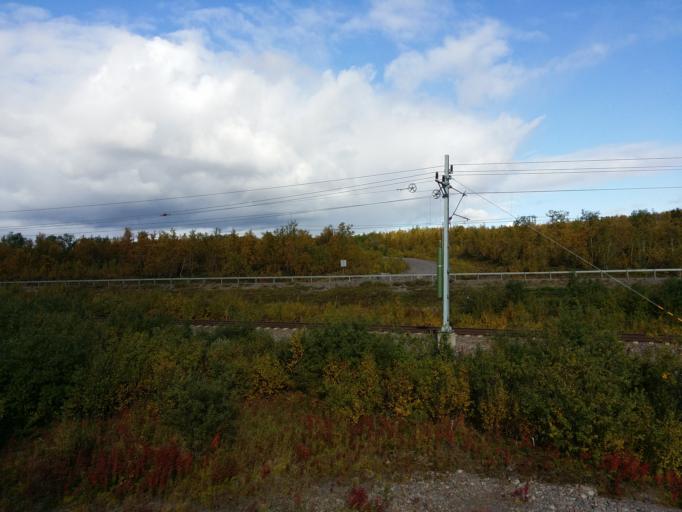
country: SE
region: Norrbotten
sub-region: Kiruna Kommun
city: Kiruna
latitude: 67.8777
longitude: 20.1670
